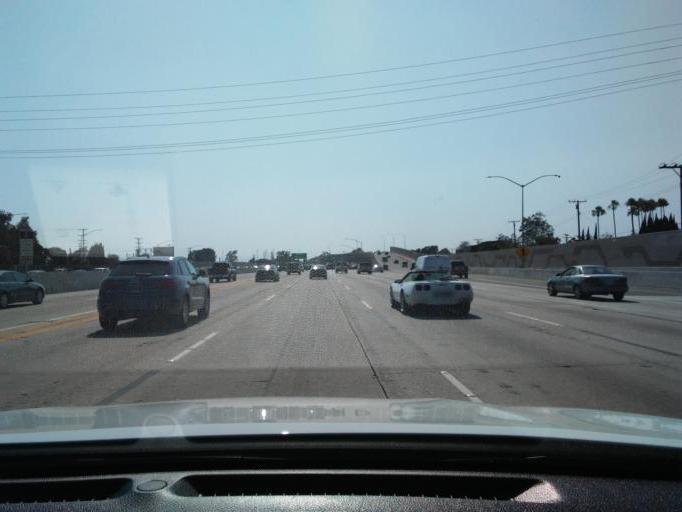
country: US
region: California
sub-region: Orange County
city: Rossmoor
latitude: 33.7746
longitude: -118.0799
